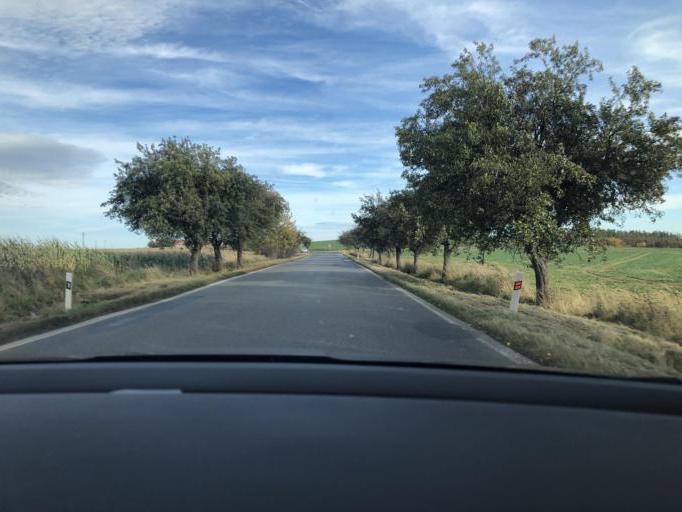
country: CZ
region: Central Bohemia
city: Divisov
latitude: 49.7881
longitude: 14.8558
